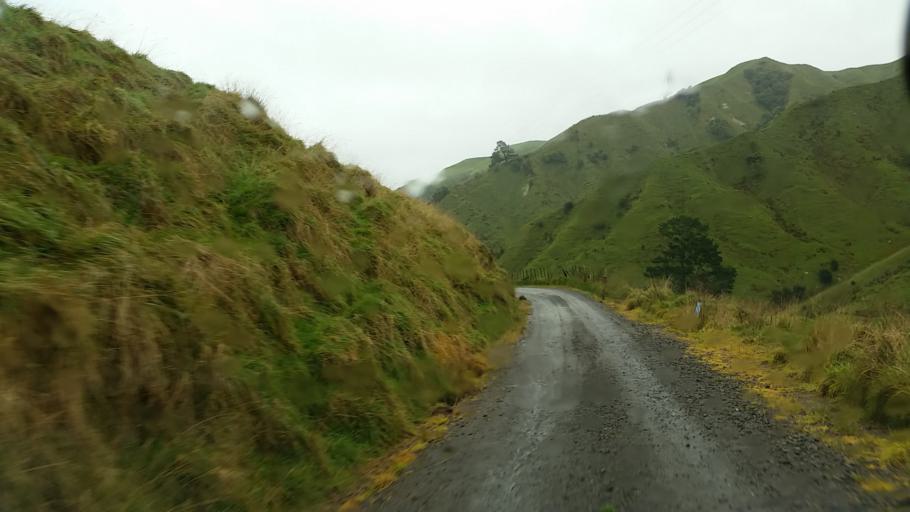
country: NZ
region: Taranaki
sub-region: South Taranaki District
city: Eltham
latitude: -39.4768
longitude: 174.4101
